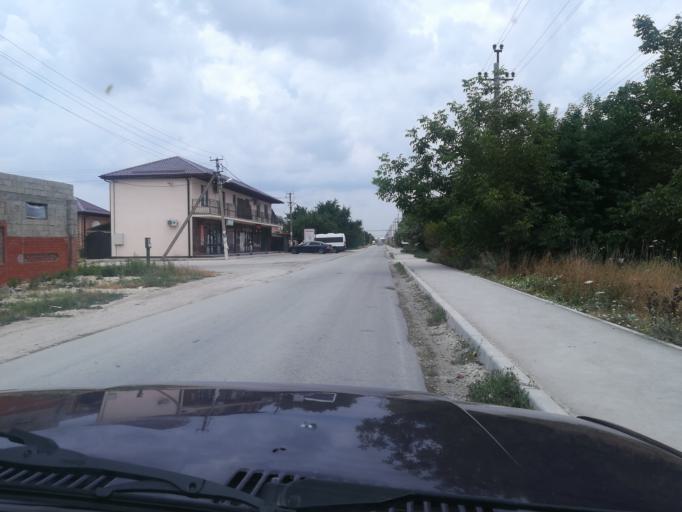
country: RU
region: Krasnodarskiy
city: Vityazevo
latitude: 45.0099
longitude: 37.2906
